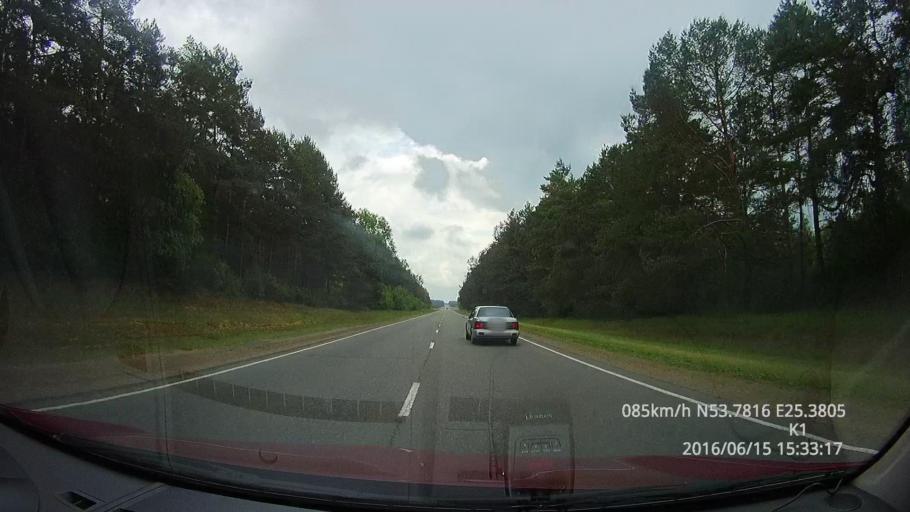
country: BY
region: Grodnenskaya
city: Lida
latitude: 53.7810
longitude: 25.3808
